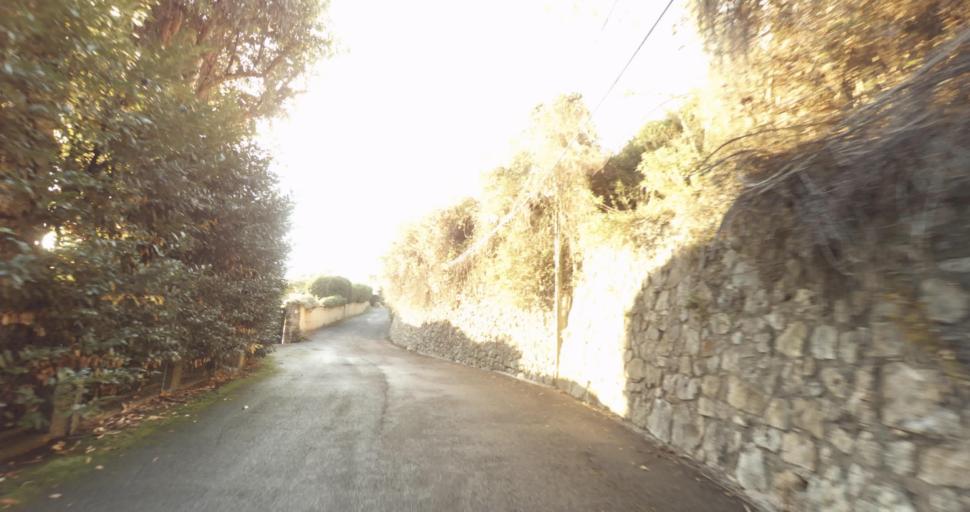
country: FR
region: Provence-Alpes-Cote d'Azur
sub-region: Departement des Alpes-Maritimes
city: Vence
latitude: 43.7334
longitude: 7.0924
